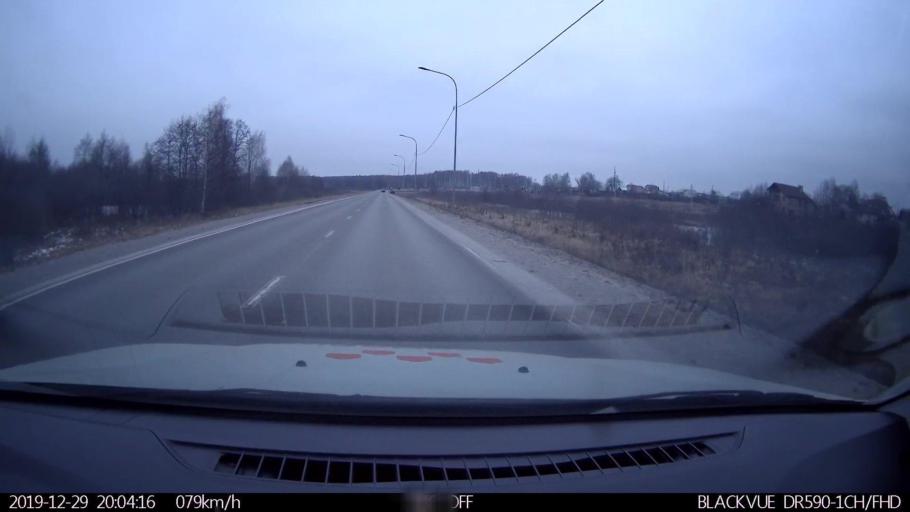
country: RU
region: Nizjnij Novgorod
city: Neklyudovo
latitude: 56.3811
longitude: 44.0111
